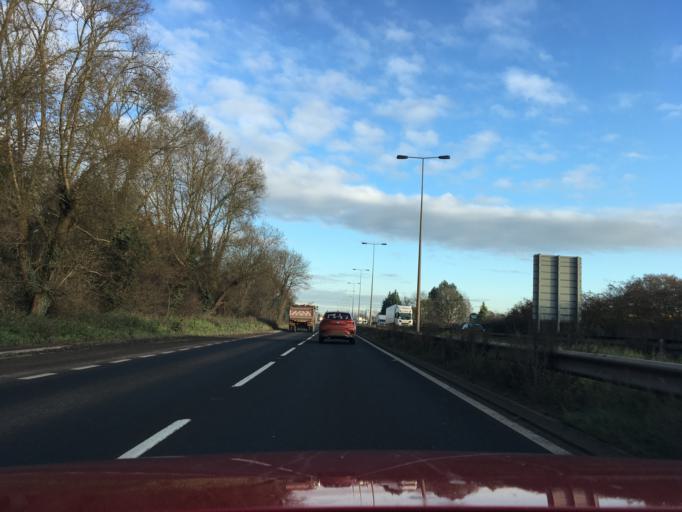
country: GB
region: England
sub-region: Staffordshire
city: Barton under Needwood
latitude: 52.7672
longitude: -1.6943
